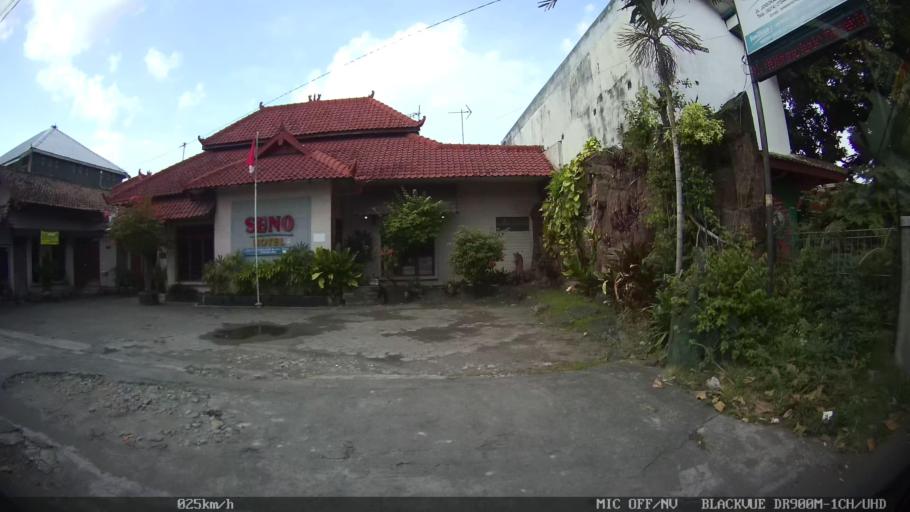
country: ID
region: Daerah Istimewa Yogyakarta
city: Kasihan
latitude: -7.8240
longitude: 110.3636
